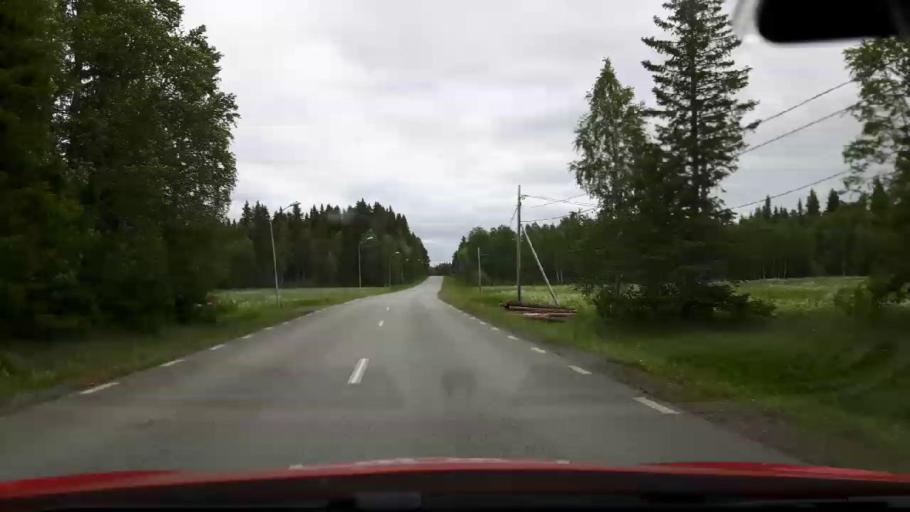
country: SE
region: Jaemtland
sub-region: OEstersunds Kommun
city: Lit
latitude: 63.6735
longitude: 15.0692
